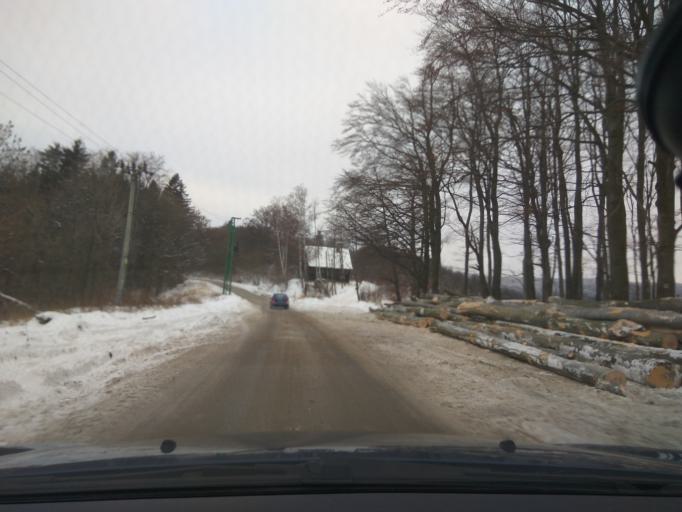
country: CZ
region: Zlin
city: Strani
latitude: 48.8460
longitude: 17.6925
